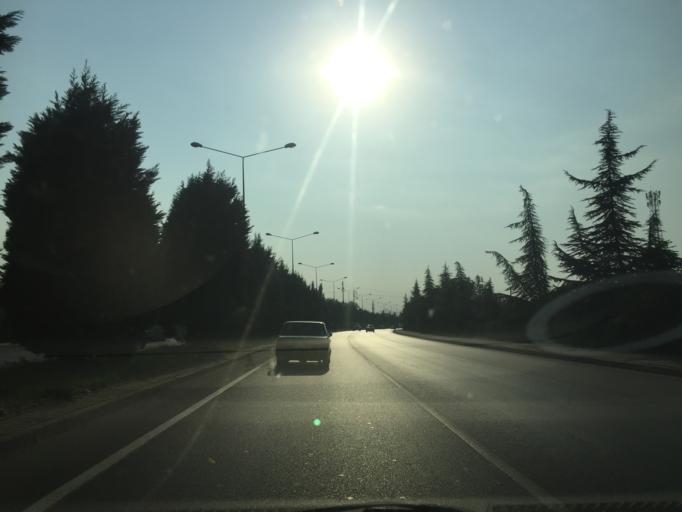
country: TR
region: Manisa
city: Salihli
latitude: 38.4895
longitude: 28.1564
